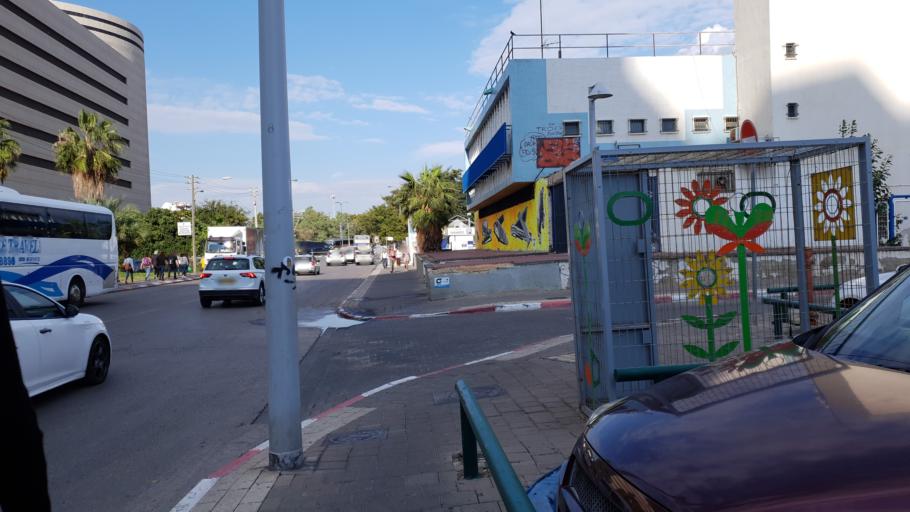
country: IL
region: Tel Aviv
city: Yafo
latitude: 32.0643
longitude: 34.7641
